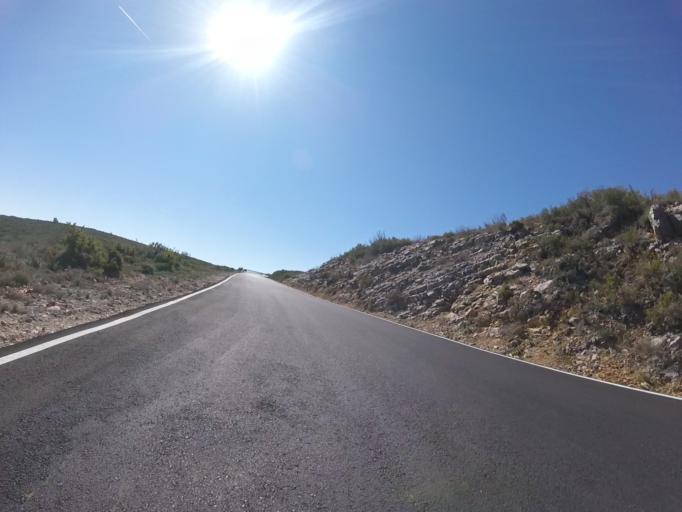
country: ES
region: Valencia
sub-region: Provincia de Castello
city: Cervera del Maestre
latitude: 40.4065
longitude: 0.2212
